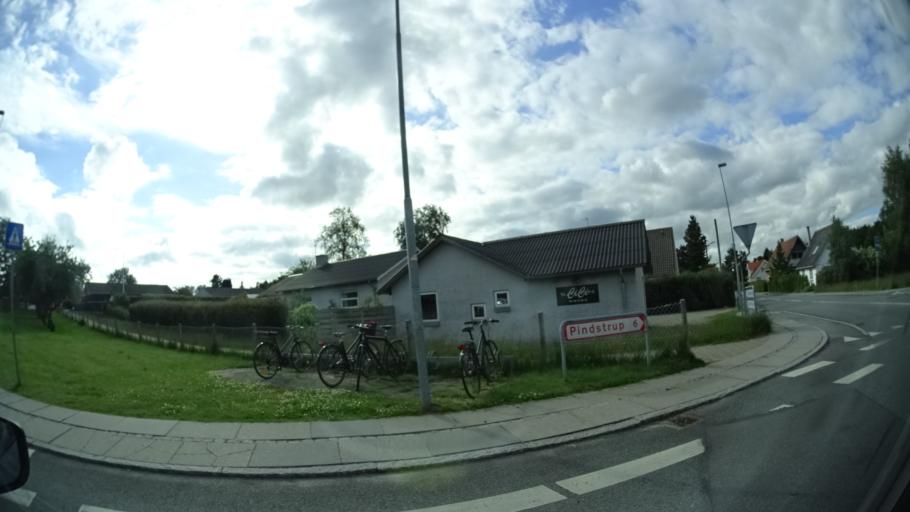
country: DK
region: Central Jutland
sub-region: Syddjurs Kommune
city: Ronde
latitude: 56.3461
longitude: 10.4549
